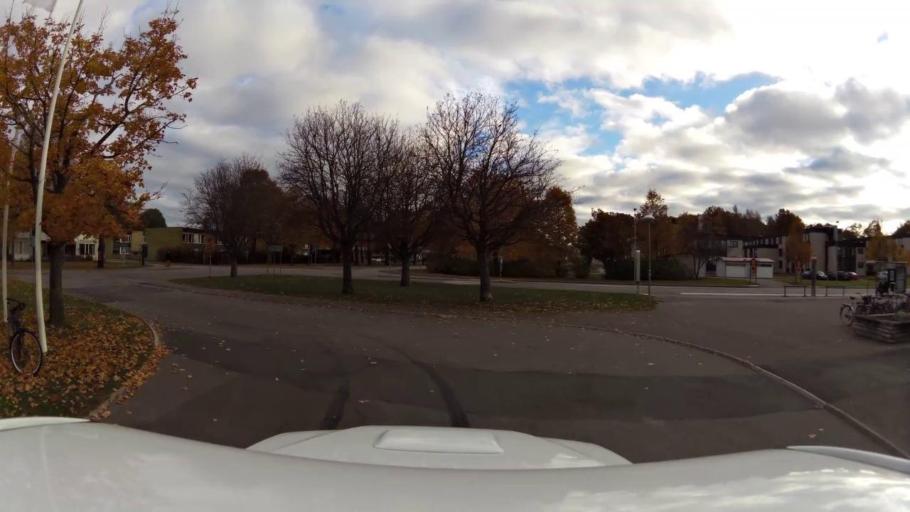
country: SE
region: OEstergoetland
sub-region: Linkopings Kommun
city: Malmslatt
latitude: 58.4085
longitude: 15.5635
